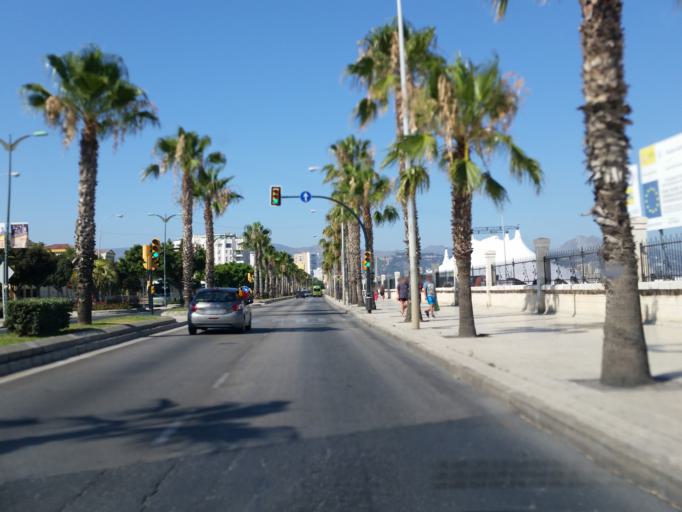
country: ES
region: Andalusia
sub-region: Provincia de Malaga
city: Malaga
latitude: 36.7058
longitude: -4.4308
